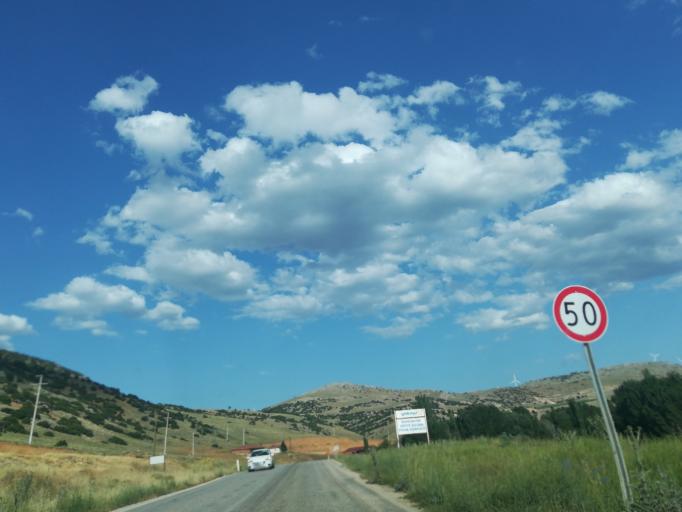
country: TR
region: Afyonkarahisar
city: Dinar
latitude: 38.0993
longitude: 30.1527
